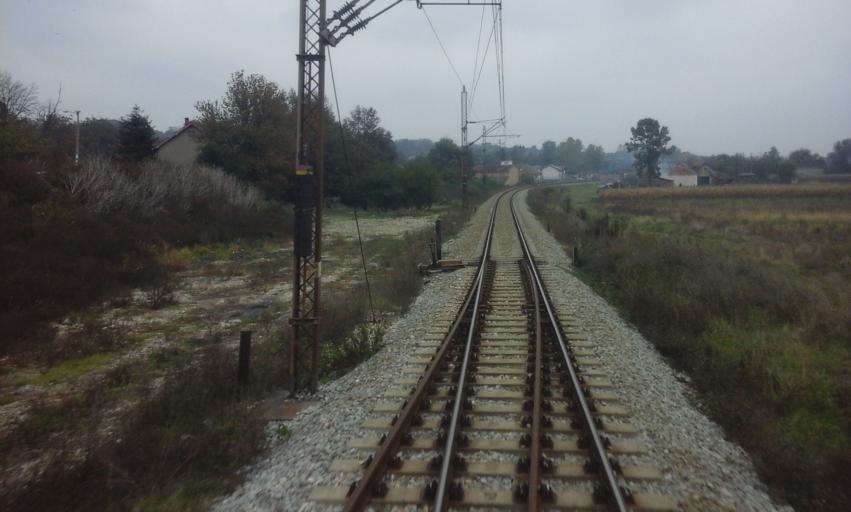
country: RS
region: Central Serbia
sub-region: Belgrade
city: Mladenovac
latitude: 44.4785
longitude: 20.6619
